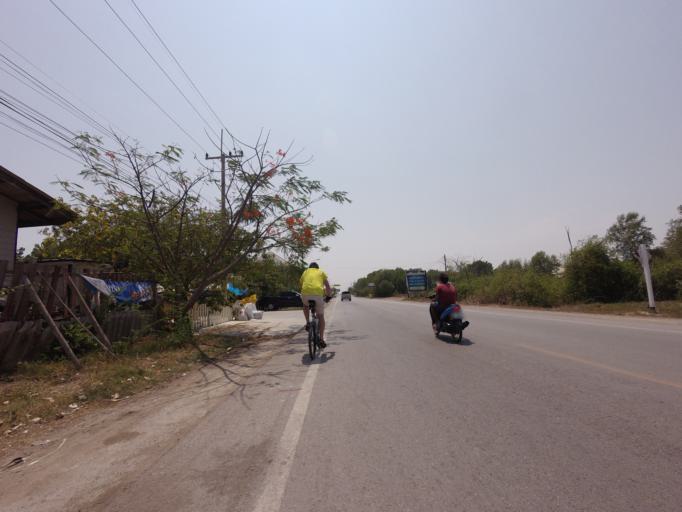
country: TH
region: Samut Sakhon
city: Samut Sakhon
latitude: 13.5144
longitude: 100.3907
